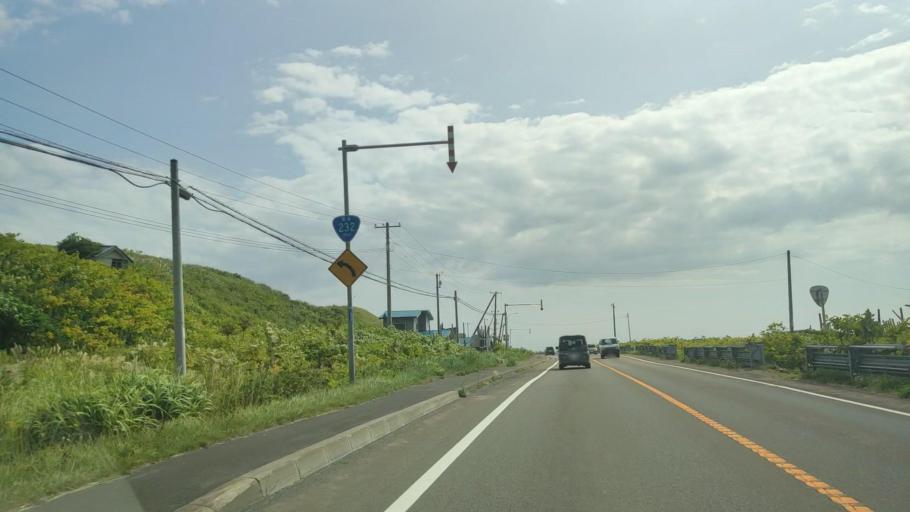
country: JP
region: Hokkaido
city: Rumoi
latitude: 44.2566
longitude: 141.6566
